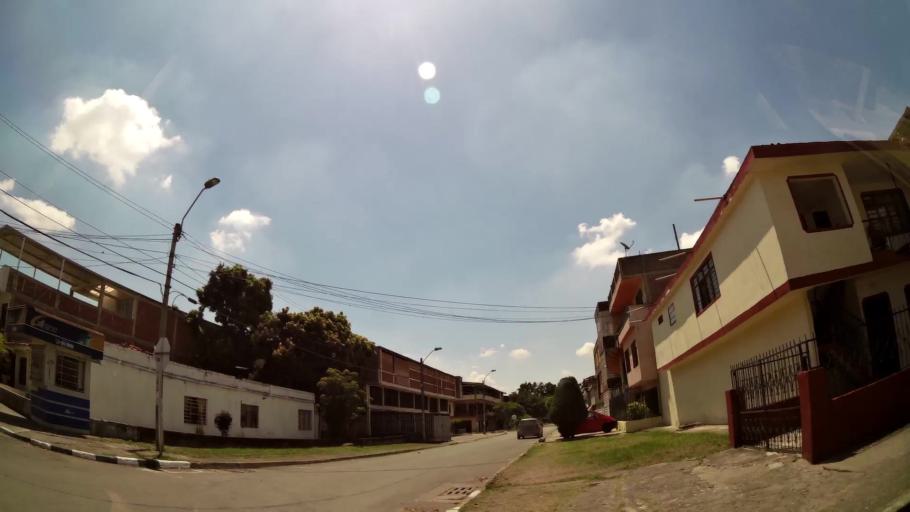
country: CO
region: Valle del Cauca
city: Cali
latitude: 3.4393
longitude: -76.4969
